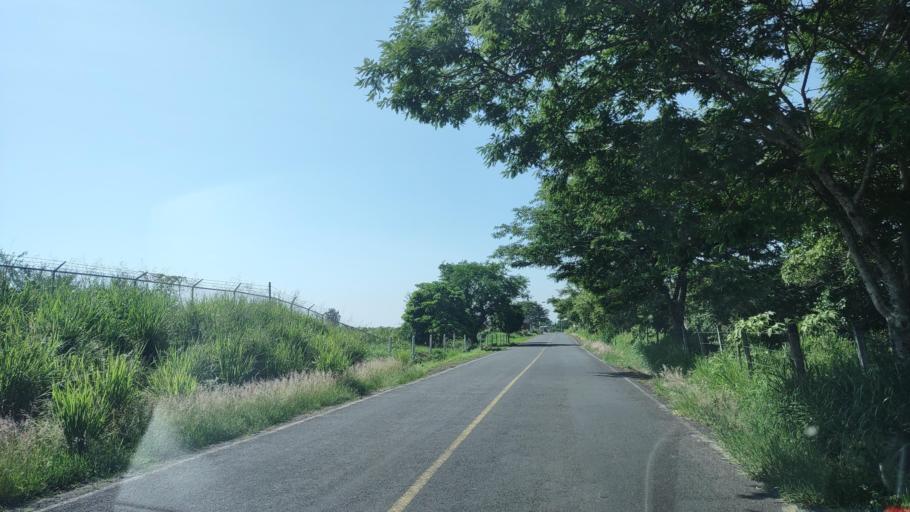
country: MX
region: Veracruz
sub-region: Emiliano Zapata
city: Dos Rios
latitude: 19.4931
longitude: -96.8230
